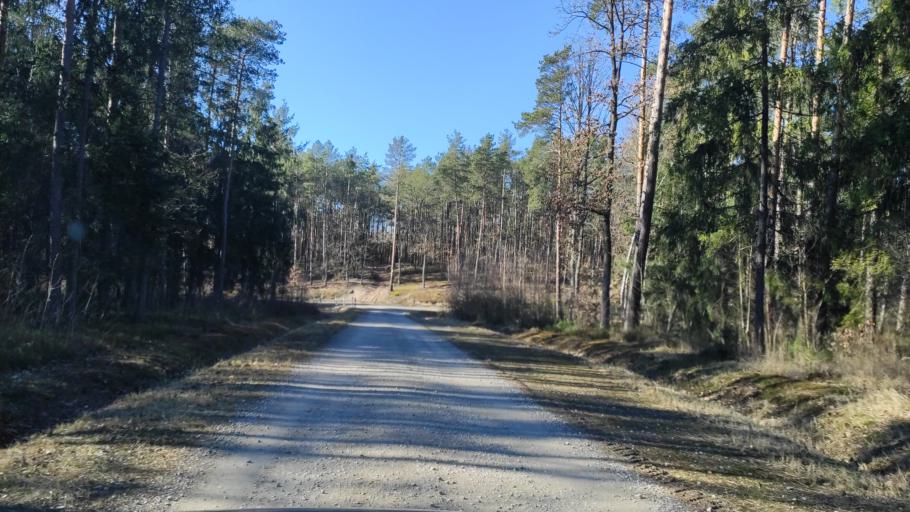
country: PL
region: Masovian Voivodeship
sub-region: Powiat radomski
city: Jedlnia-Letnisko
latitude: 51.4736
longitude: 21.2970
